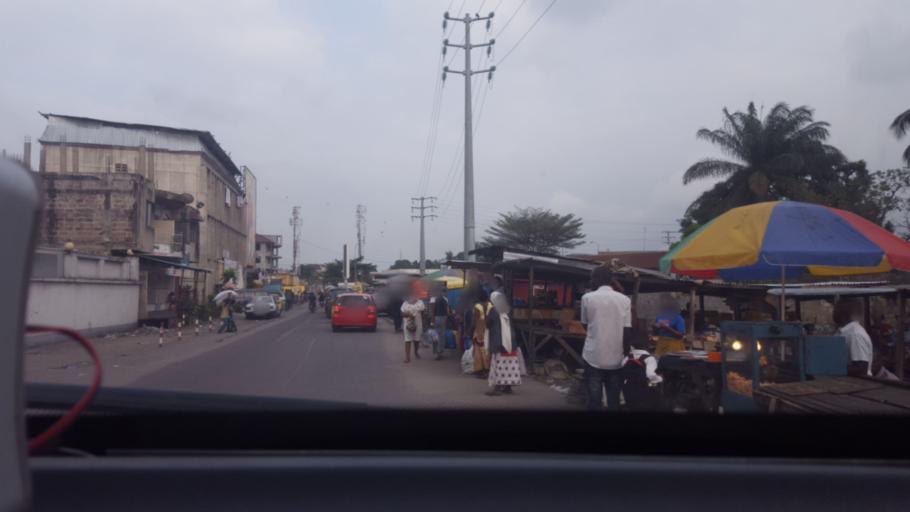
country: CD
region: Kinshasa
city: Kinshasa
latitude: -4.3345
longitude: 15.3159
